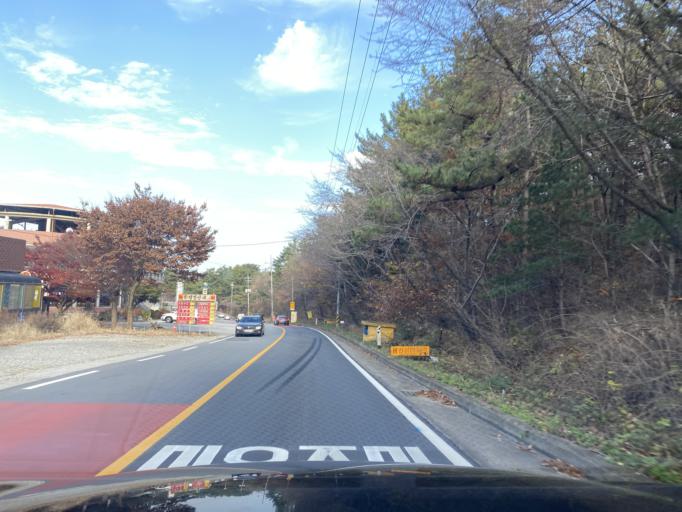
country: KR
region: Chungcheongnam-do
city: Hongsung
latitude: 36.6703
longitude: 126.6407
